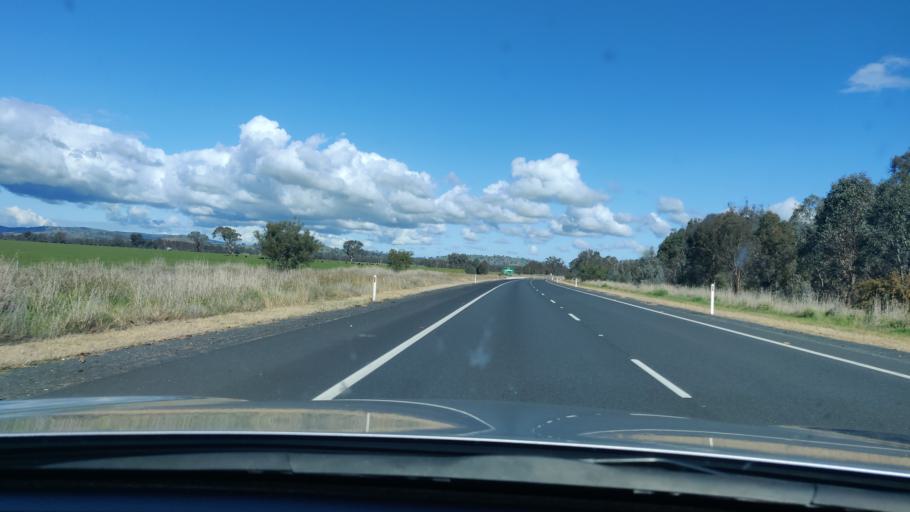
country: AU
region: New South Wales
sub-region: Greater Hume Shire
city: Holbrook
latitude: -35.7441
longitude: 147.3017
